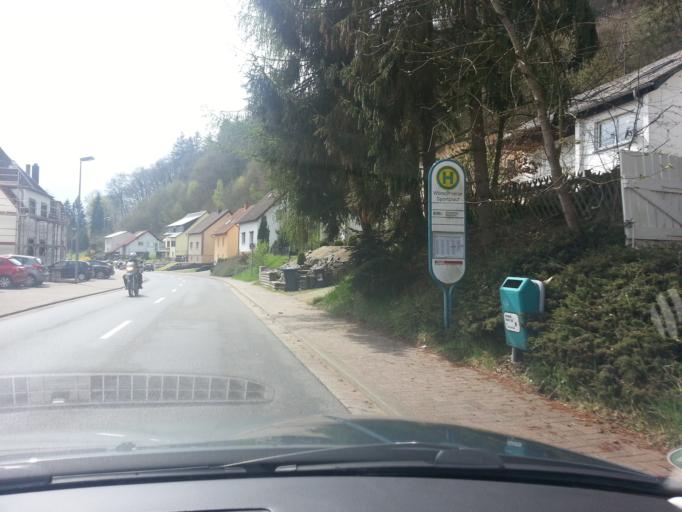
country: DE
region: Saarland
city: Homburg
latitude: 49.2821
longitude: 7.3079
